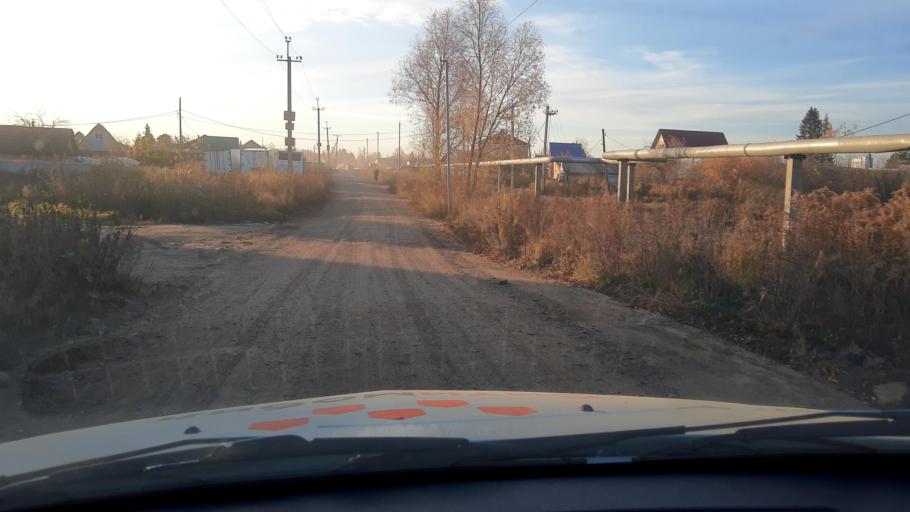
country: RU
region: Bashkortostan
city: Ufa
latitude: 54.8160
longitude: 56.1544
